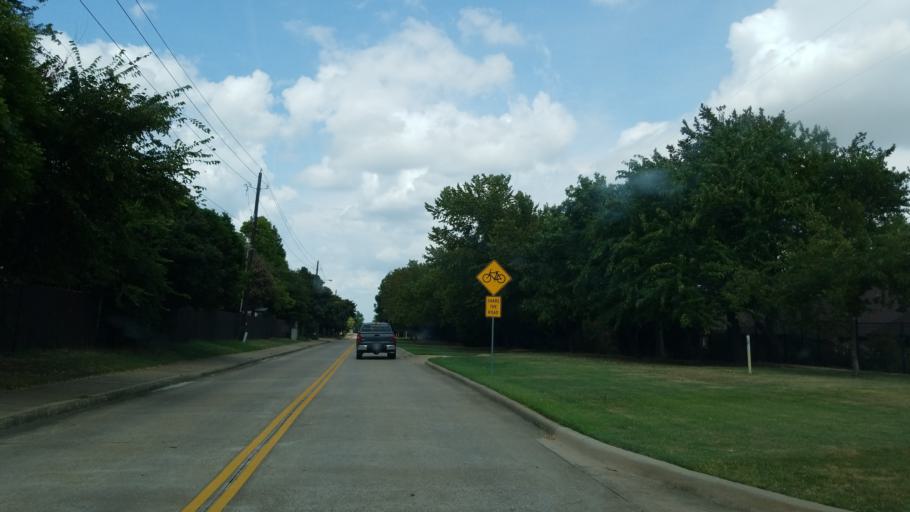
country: US
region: Texas
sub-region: Tarrant County
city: Euless
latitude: 32.8829
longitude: -97.0824
